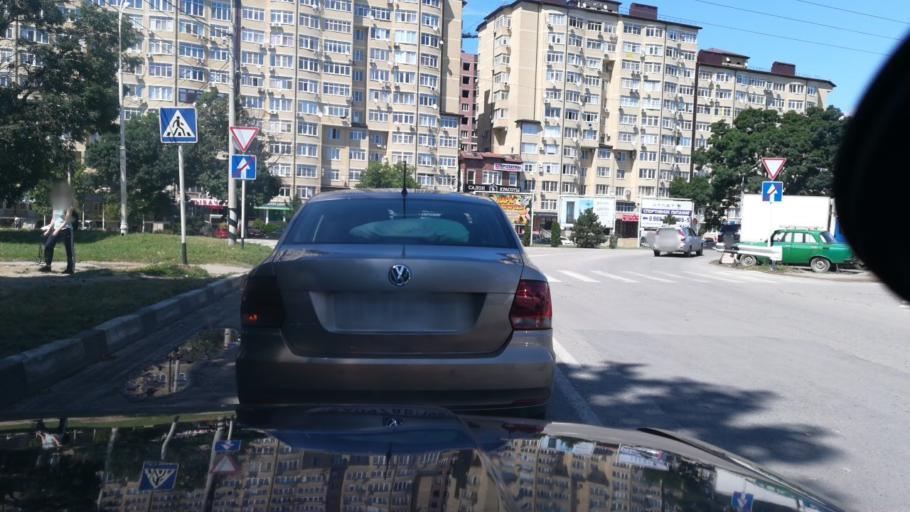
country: RU
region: Krasnodarskiy
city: Anapa
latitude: 44.8988
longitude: 37.3435
